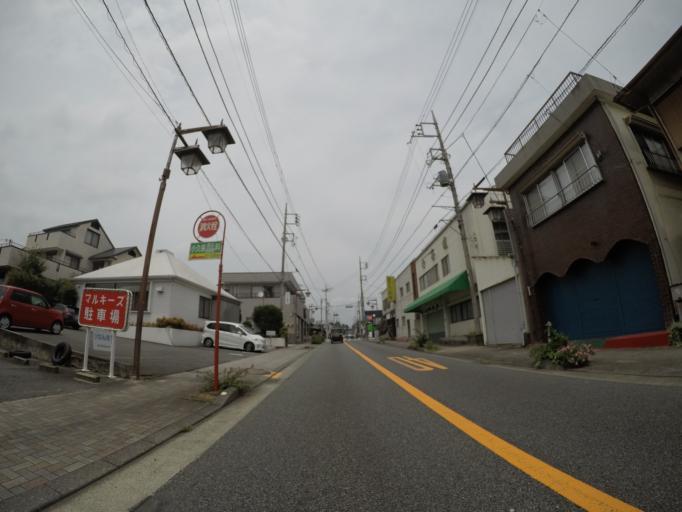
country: JP
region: Shizuoka
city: Fujinomiya
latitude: 35.2278
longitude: 138.6068
